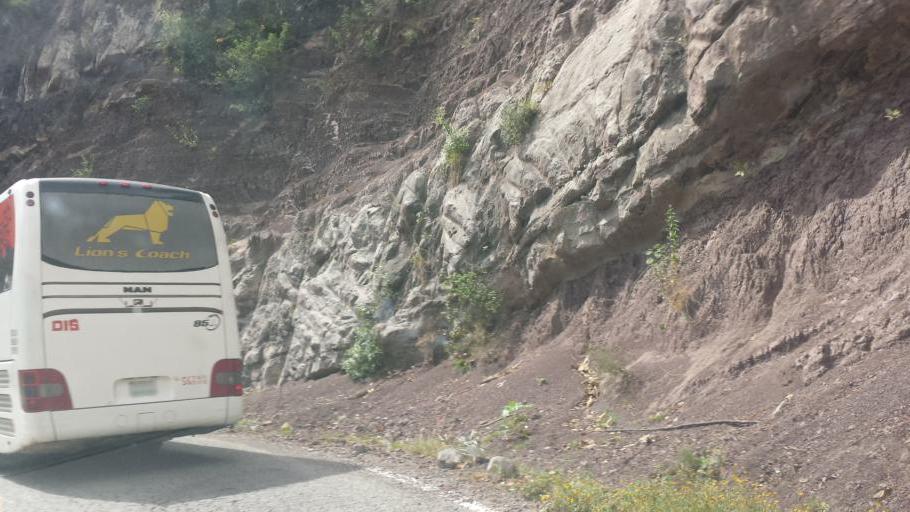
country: MX
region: Oaxaca
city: San Francisco Sola
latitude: 16.4535
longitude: -97.0337
